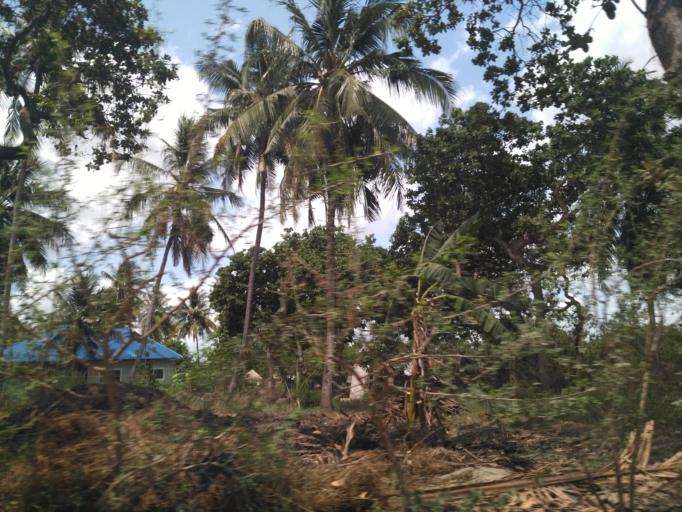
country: TZ
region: Dar es Salaam
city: Dar es Salaam
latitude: -6.8795
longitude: 39.3406
